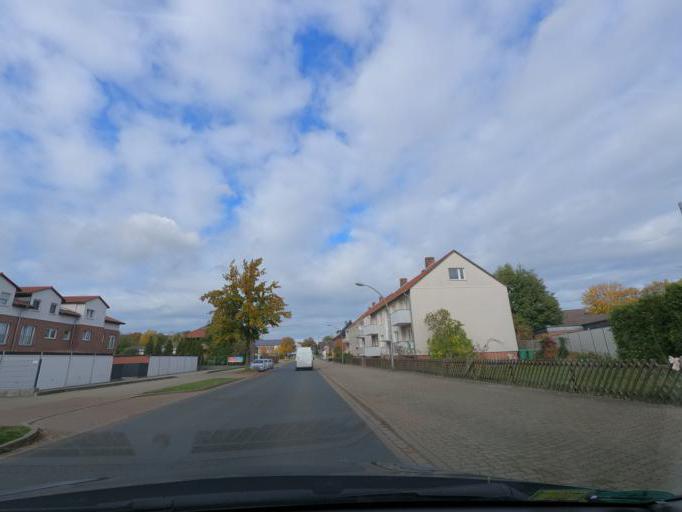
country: DE
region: Lower Saxony
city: Leiferde
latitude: 52.1902
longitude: 10.4801
